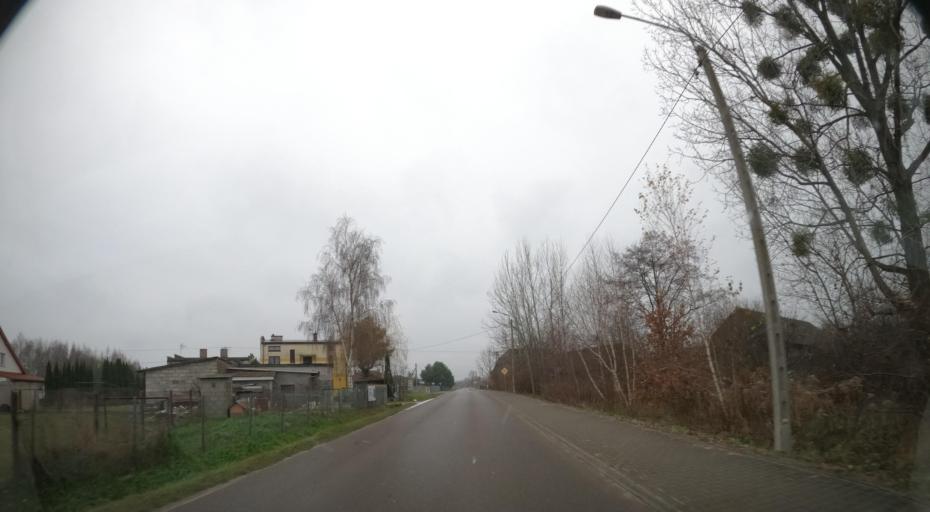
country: PL
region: Masovian Voivodeship
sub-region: Powiat radomski
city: Skaryszew
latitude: 51.3875
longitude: 21.2586
